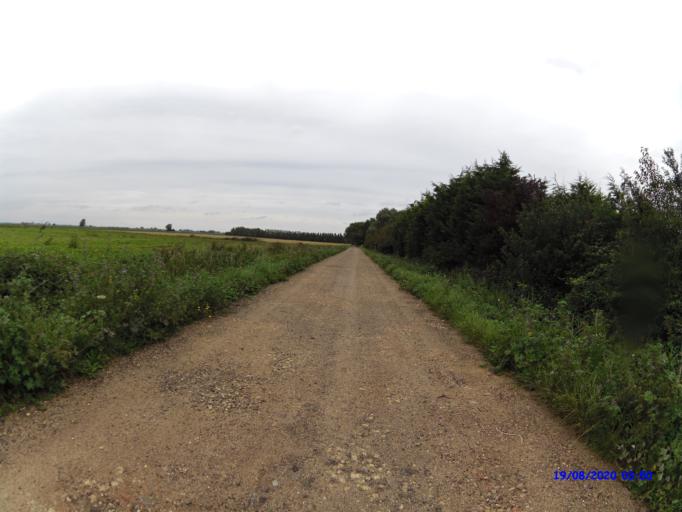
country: GB
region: England
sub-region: Cambridgeshire
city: Ramsey
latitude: 52.4635
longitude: -0.1115
